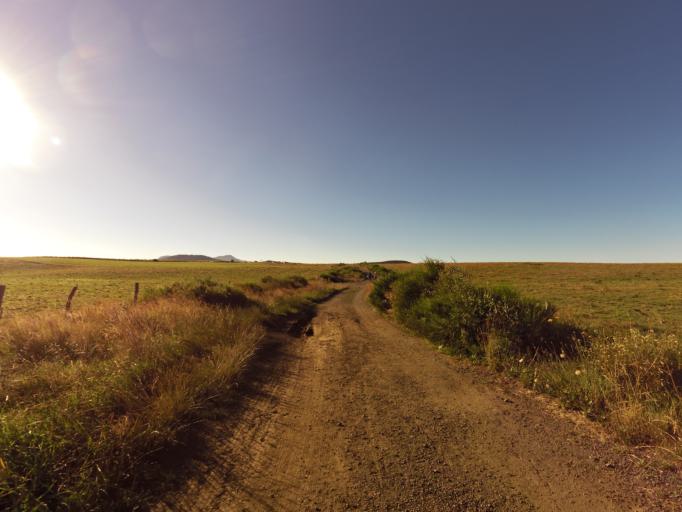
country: FR
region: Auvergne
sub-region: Departement du Puy-de-Dome
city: Mont-Dore
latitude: 45.4709
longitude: 2.9228
